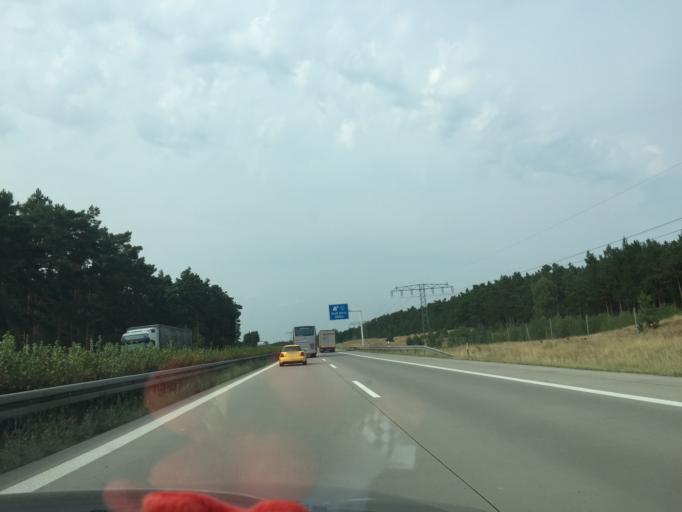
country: DE
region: Brandenburg
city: Schwerin
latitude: 52.1444
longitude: 13.6490
